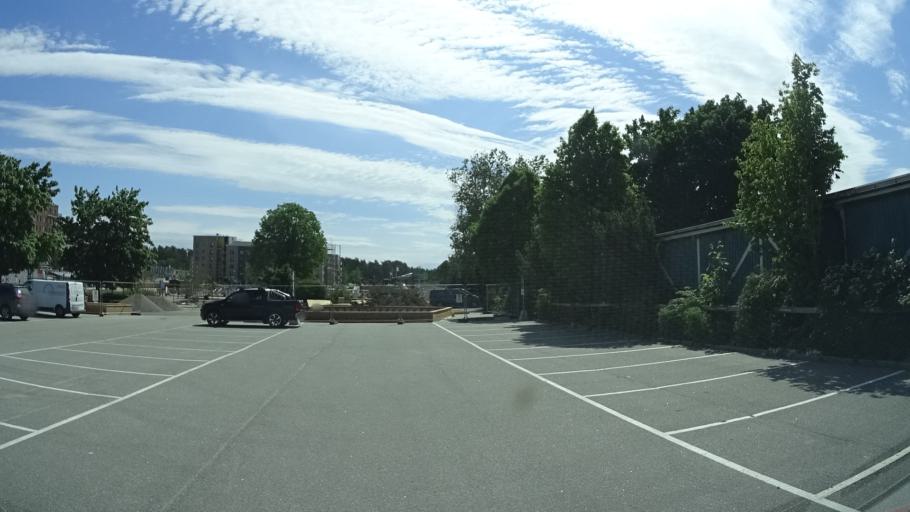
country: SE
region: Stockholm
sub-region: Taby Kommun
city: Taby
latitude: 59.4448
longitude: 18.0846
